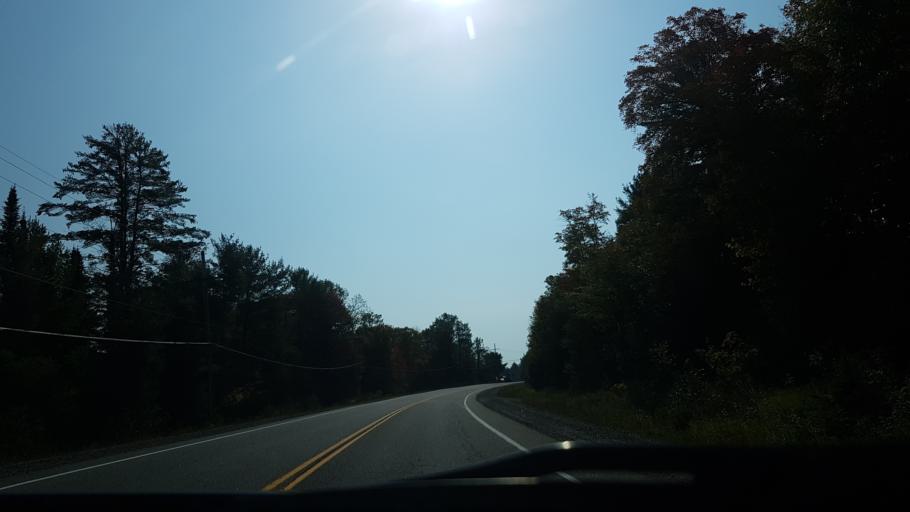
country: CA
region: Ontario
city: Bracebridge
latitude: 44.9890
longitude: -79.2779
